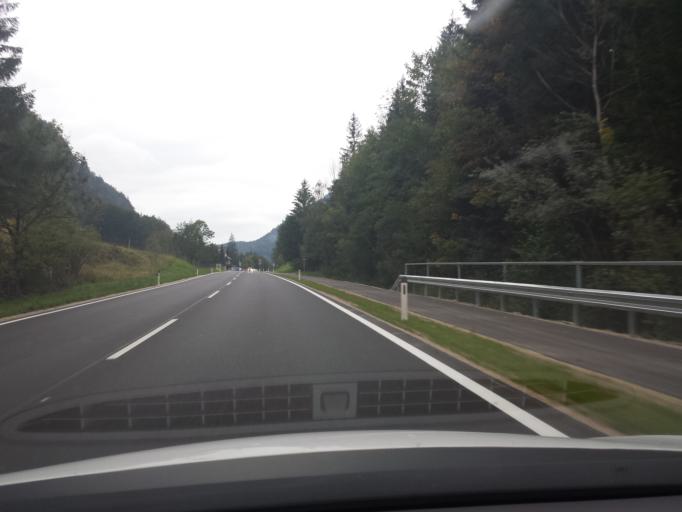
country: AT
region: Salzburg
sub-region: Politischer Bezirk Salzburg-Umgebung
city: Fuschl am See
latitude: 47.7895
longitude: 13.3363
